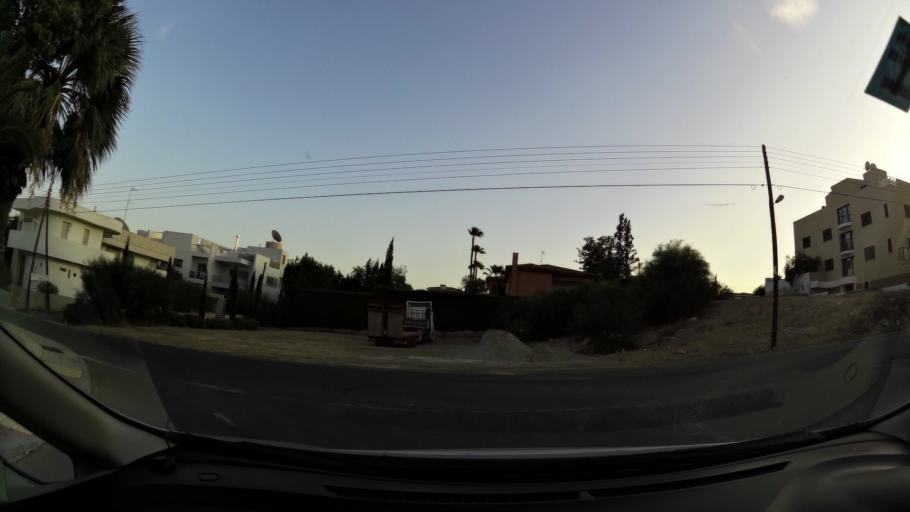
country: CY
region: Lefkosia
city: Nicosia
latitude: 35.1627
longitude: 33.3224
